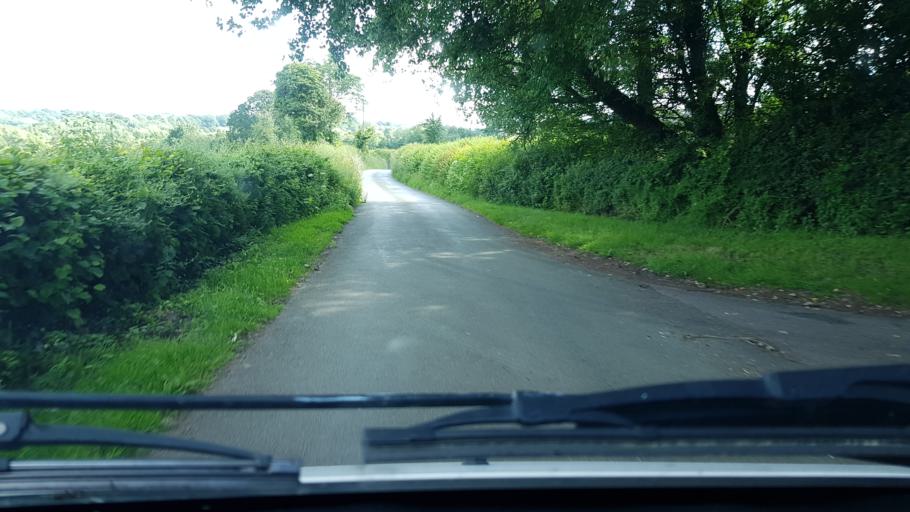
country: GB
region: England
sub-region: Shropshire
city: Romsley
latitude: 52.4446
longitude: -2.3003
